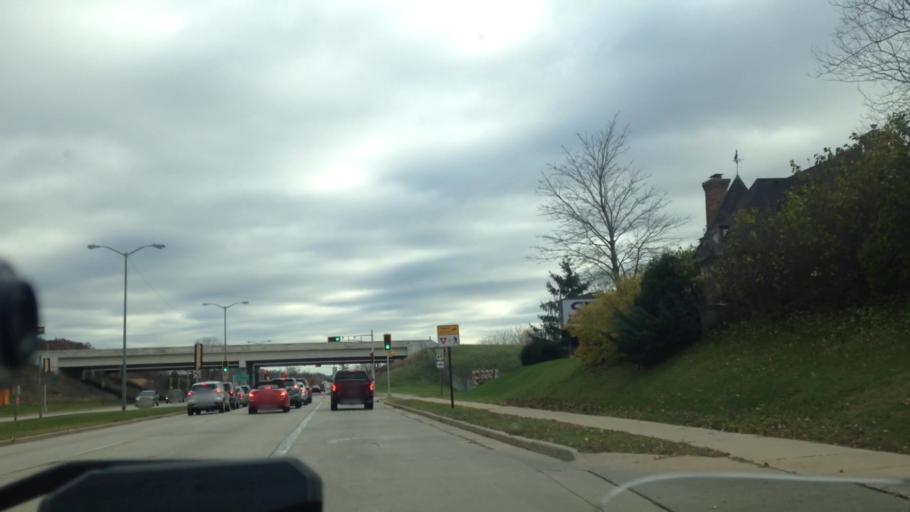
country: US
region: Wisconsin
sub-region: Washington County
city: West Bend
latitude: 43.4271
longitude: -88.2103
